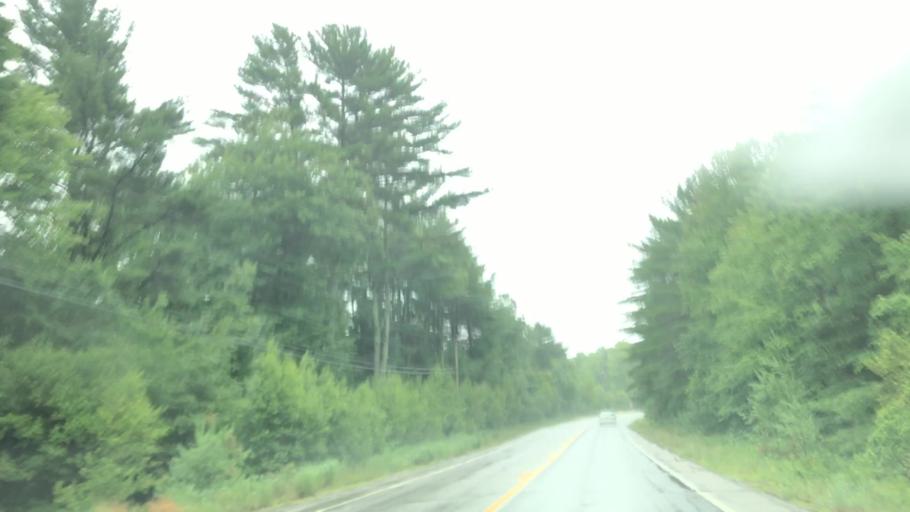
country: US
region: Maine
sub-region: York County
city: North Berwick
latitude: 43.2997
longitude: -70.7676
